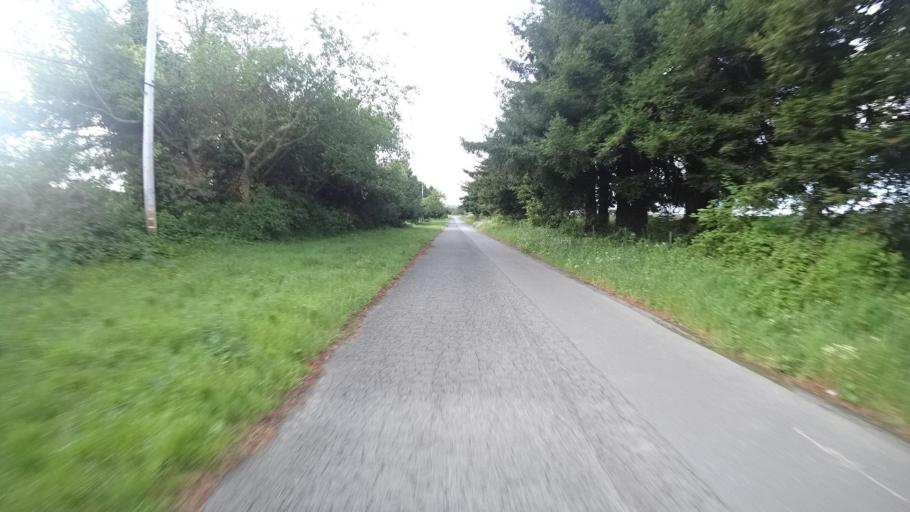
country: US
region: California
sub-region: Humboldt County
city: McKinleyville
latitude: 40.9114
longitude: -124.0899
